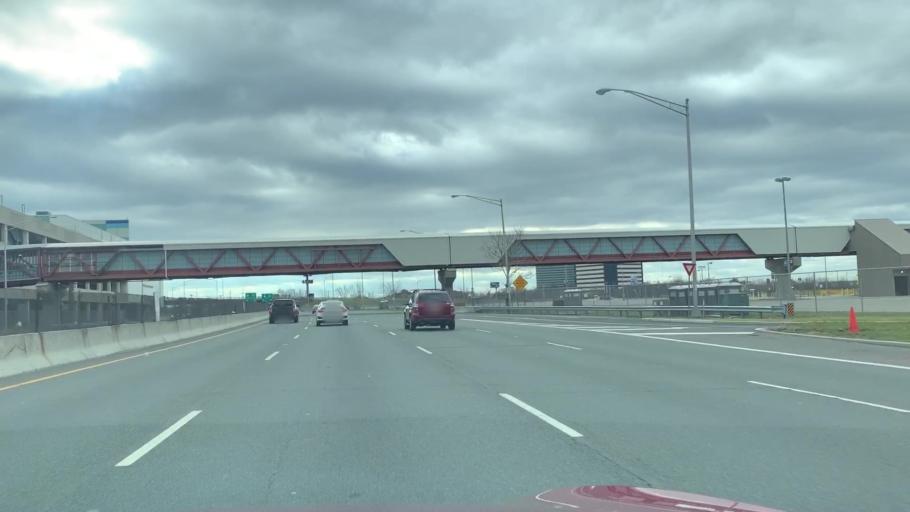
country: US
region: New Jersey
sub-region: Hudson County
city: Secaucus
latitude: 40.8114
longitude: -74.0714
